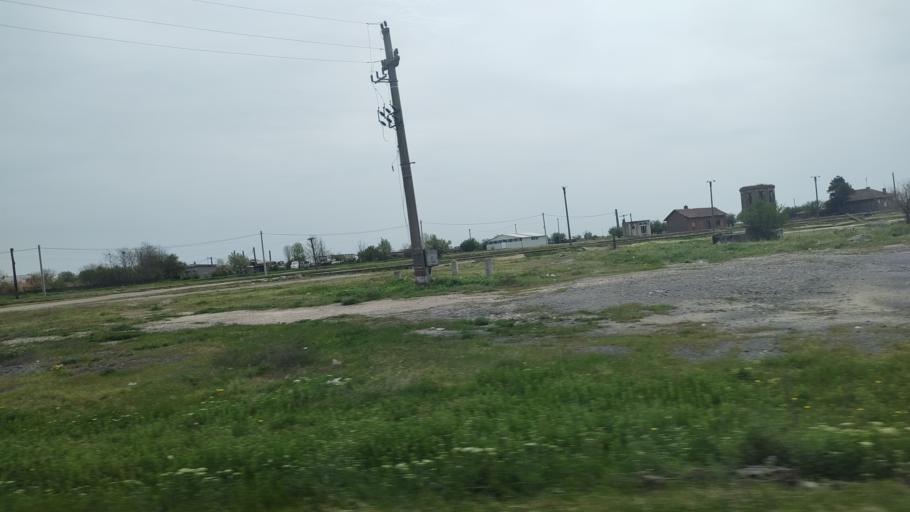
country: RO
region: Constanta
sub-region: Comuna Ciocarlia
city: Ciocarlia
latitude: 44.1020
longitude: 28.2773
